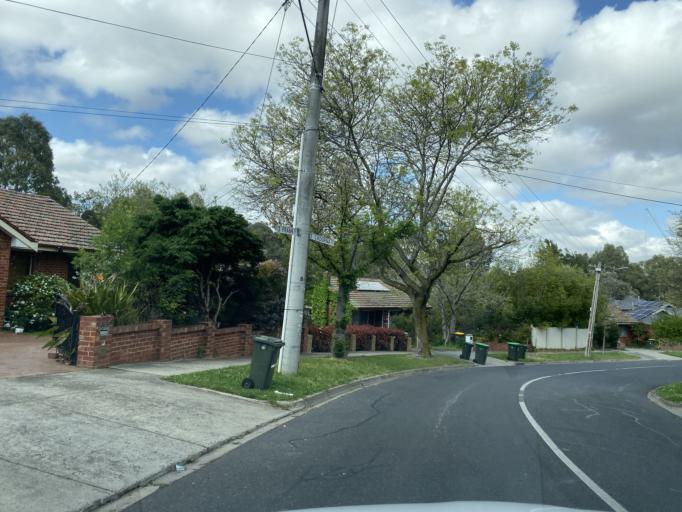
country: AU
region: Victoria
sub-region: Whitehorse
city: Burwood
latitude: -37.8420
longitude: 145.1174
